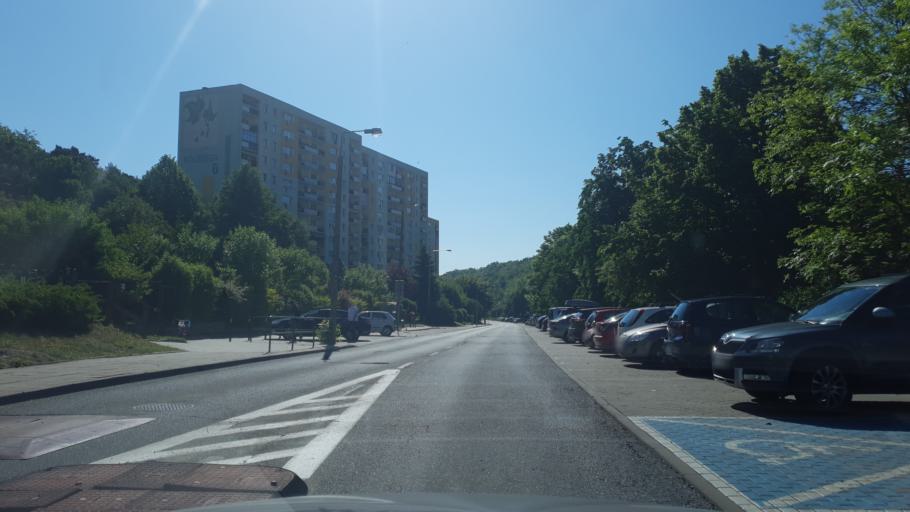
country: PL
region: Pomeranian Voivodeship
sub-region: Sopot
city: Sopot
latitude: 54.4574
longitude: 18.5369
